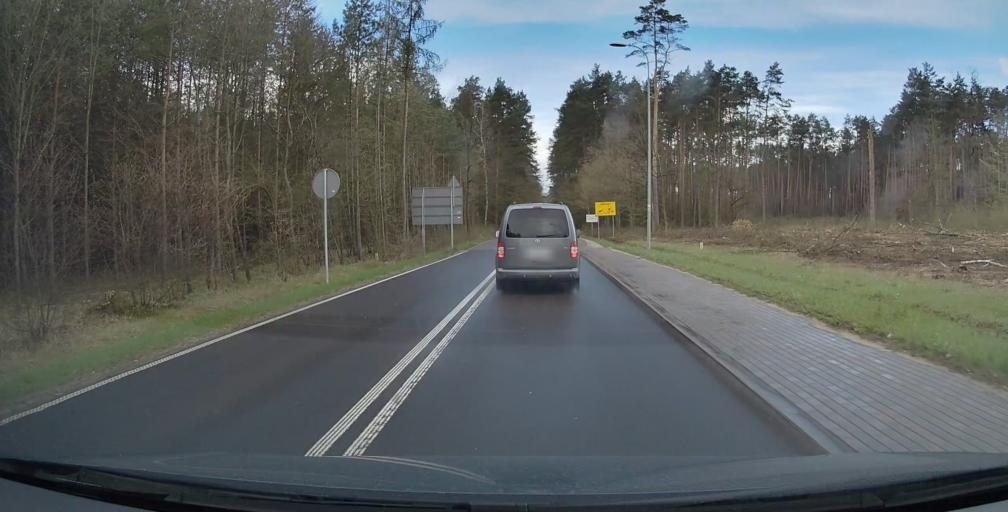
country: PL
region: Masovian Voivodeship
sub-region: Powiat wyszkowski
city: Branszczyk
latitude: 52.6719
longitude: 21.5971
